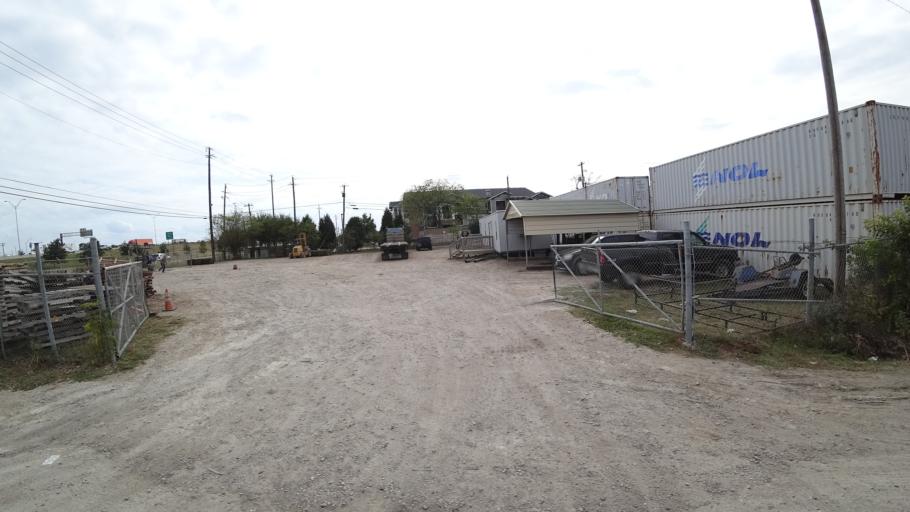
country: US
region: Texas
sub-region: Travis County
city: Wells Branch
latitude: 30.4437
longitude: -97.6687
